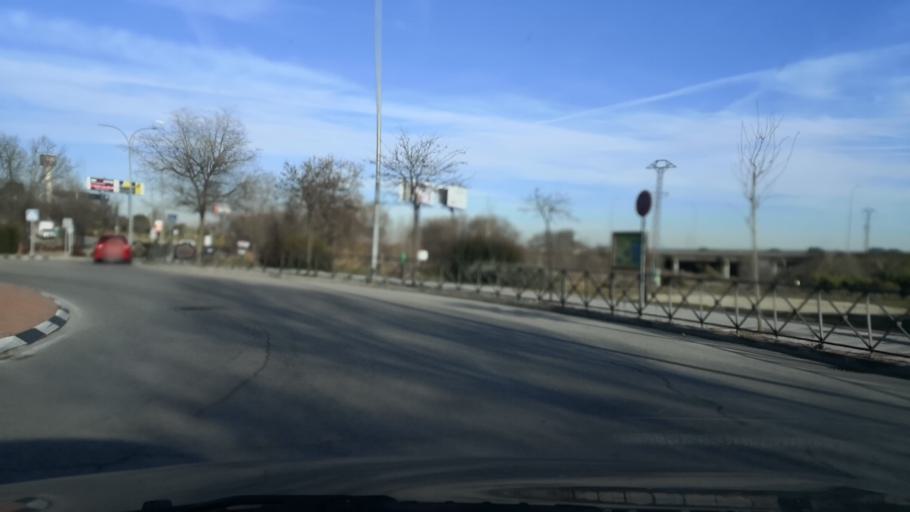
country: ES
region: Madrid
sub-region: Provincia de Madrid
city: San Sebastian de los Reyes
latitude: 40.5378
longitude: -3.6133
